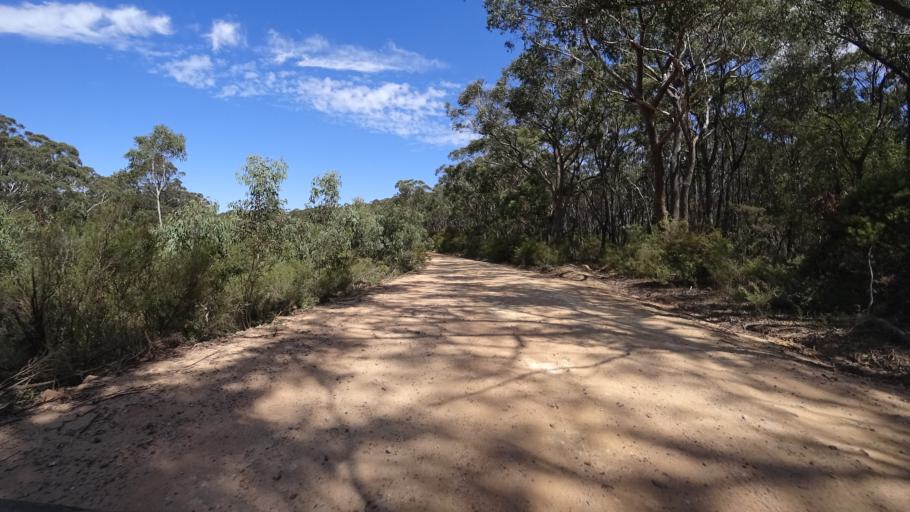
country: AU
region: New South Wales
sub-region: Lithgow
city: Lithgow
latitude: -33.3205
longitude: 150.2458
